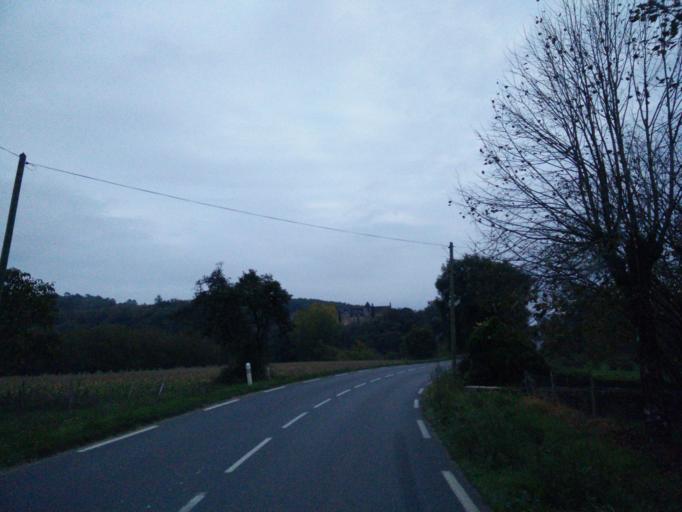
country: FR
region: Aquitaine
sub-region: Departement de la Dordogne
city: Carsac-Aillac
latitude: 44.8278
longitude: 1.2861
